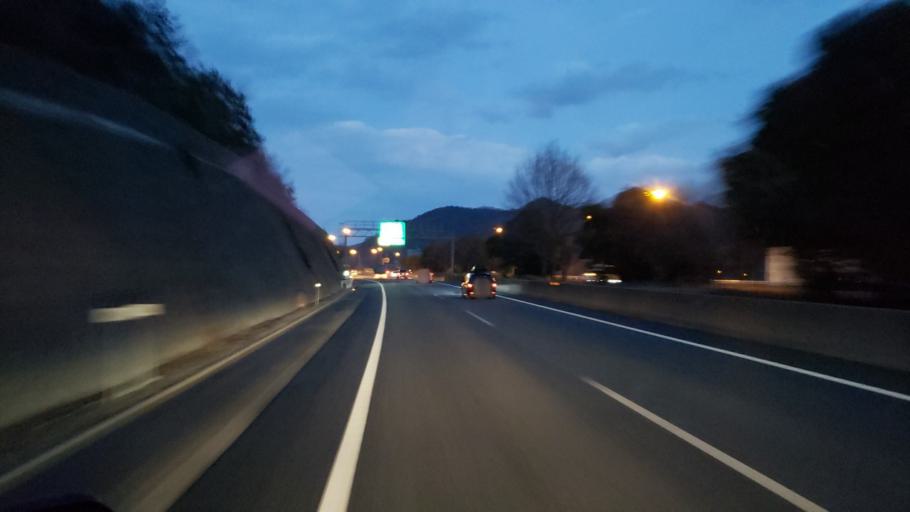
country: JP
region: Hyogo
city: Kakogawacho-honmachi
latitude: 34.8484
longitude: 134.8281
